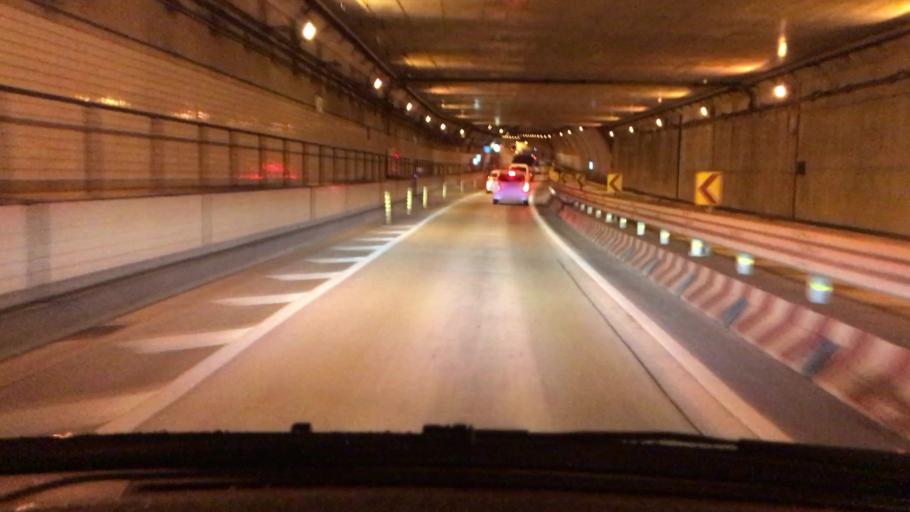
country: JP
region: Hyogo
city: Kobe
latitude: 34.6994
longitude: 135.2000
